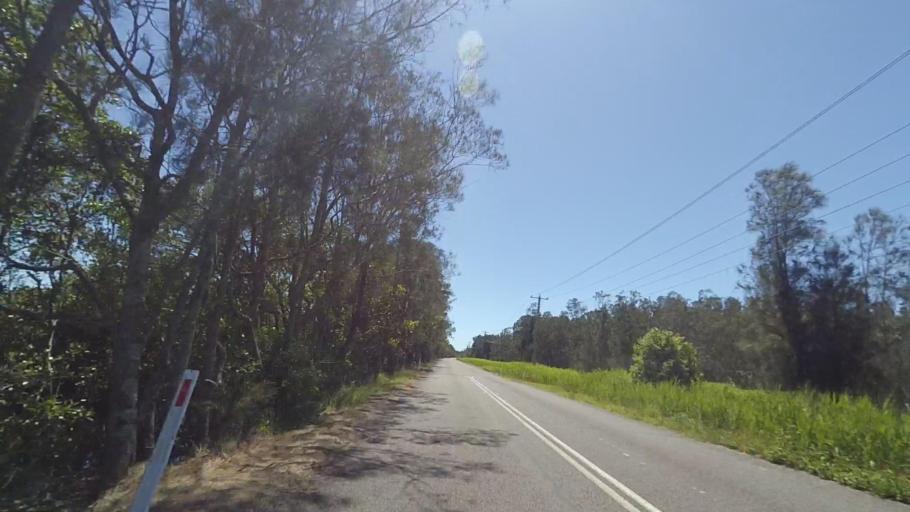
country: AU
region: New South Wales
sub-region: Port Stephens Shire
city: Medowie
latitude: -32.7803
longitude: 151.9568
